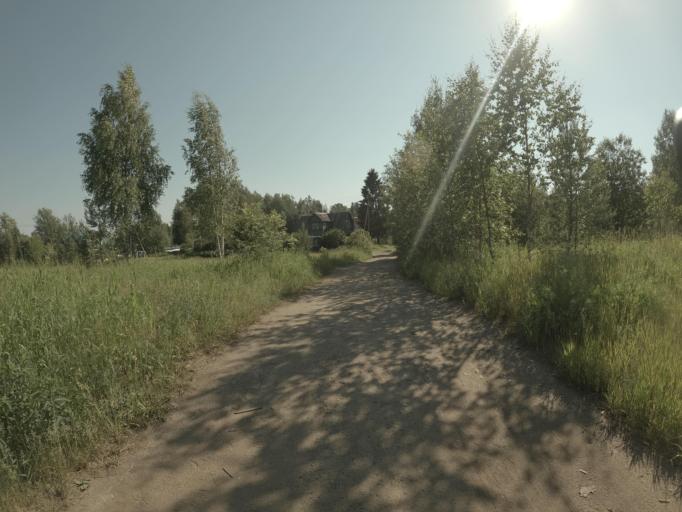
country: RU
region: Leningrad
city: Yakovlevo
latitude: 60.4669
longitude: 29.2830
